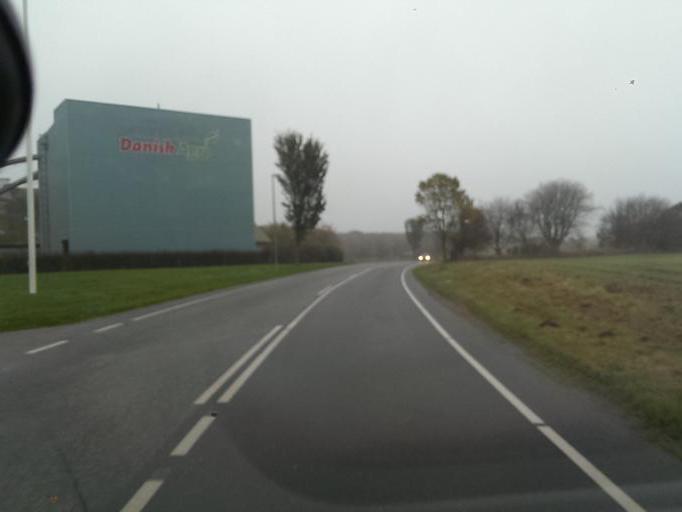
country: DK
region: South Denmark
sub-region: Esbjerg Kommune
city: Bramming
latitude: 55.4617
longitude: 8.7153
